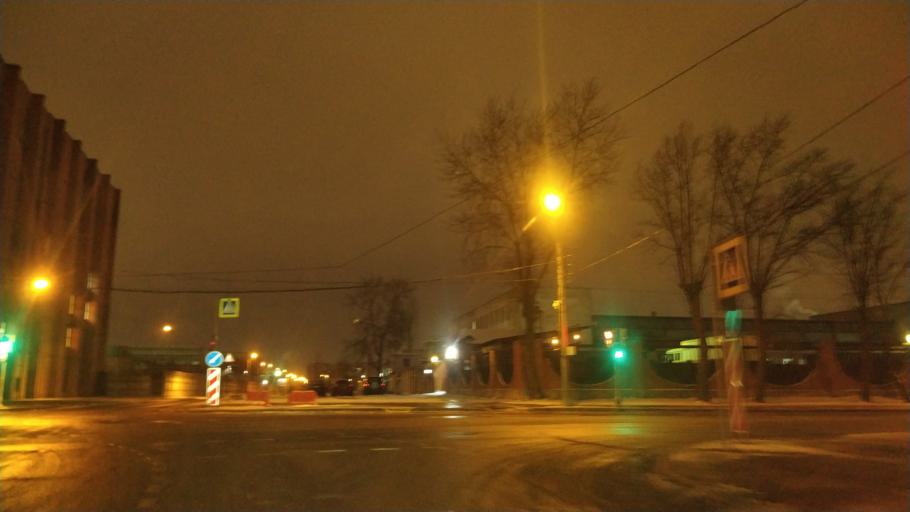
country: RU
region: St.-Petersburg
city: Kupchino
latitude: 59.8815
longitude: 30.3385
